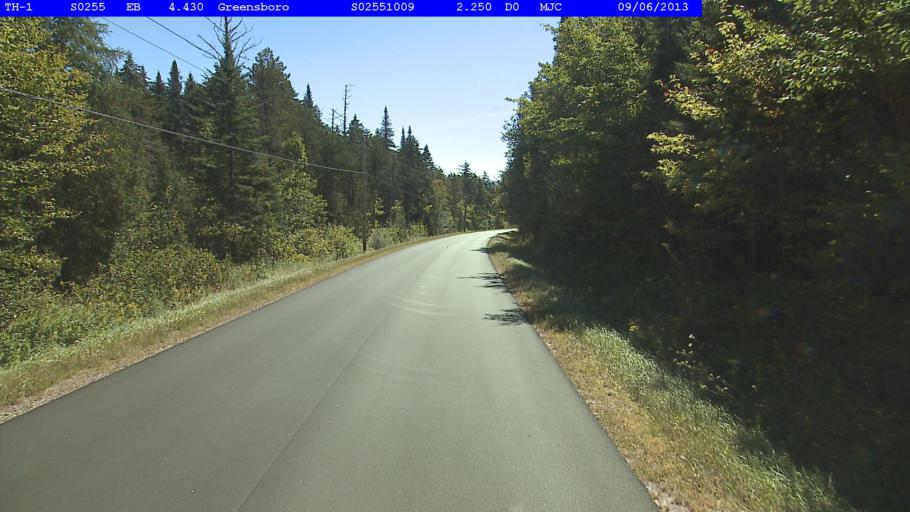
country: US
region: Vermont
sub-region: Caledonia County
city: Hardwick
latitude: 44.6105
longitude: -72.3200
